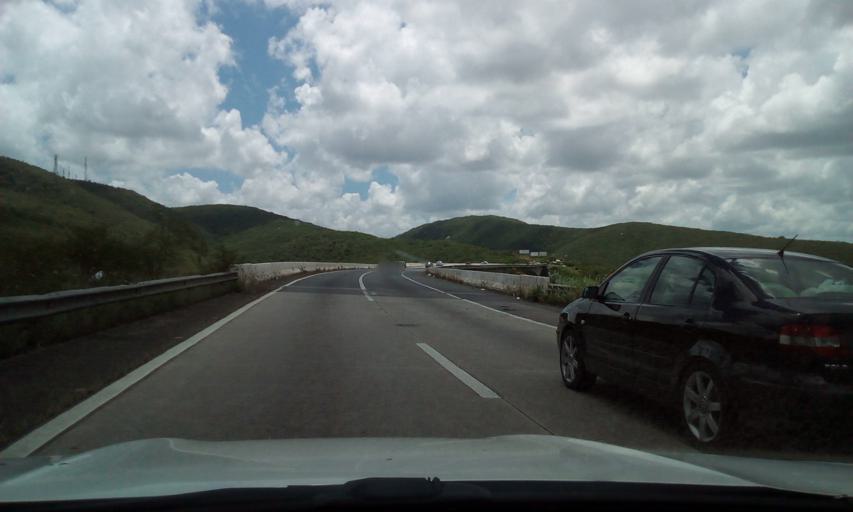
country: BR
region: Pernambuco
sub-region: Pombos
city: Pombos
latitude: -8.1675
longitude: -35.4537
